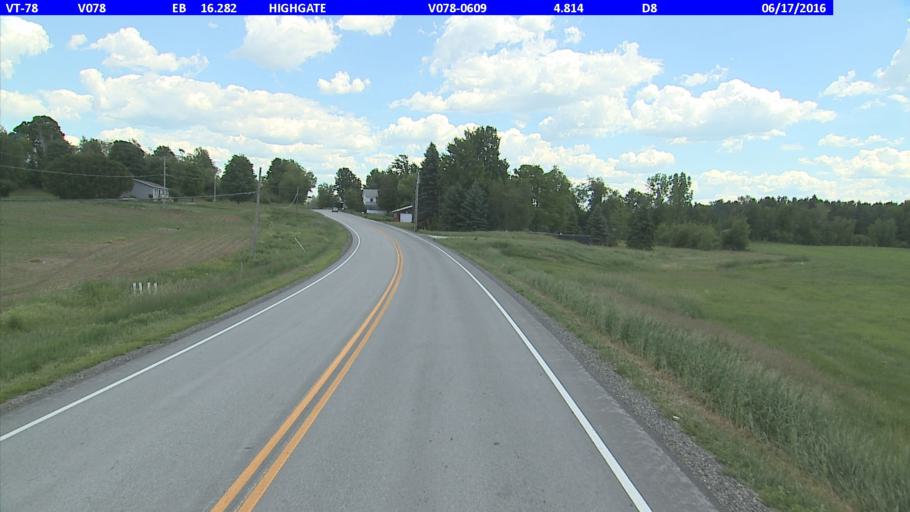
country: US
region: Vermont
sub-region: Franklin County
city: Swanton
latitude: 44.9452
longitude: -73.0132
